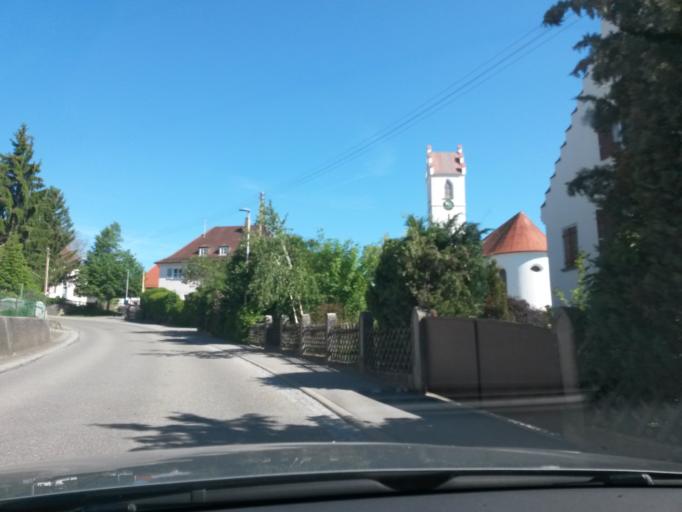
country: DE
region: Baden-Wuerttemberg
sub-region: Tuebingen Region
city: Kanzach
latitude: 48.0792
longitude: 9.5563
